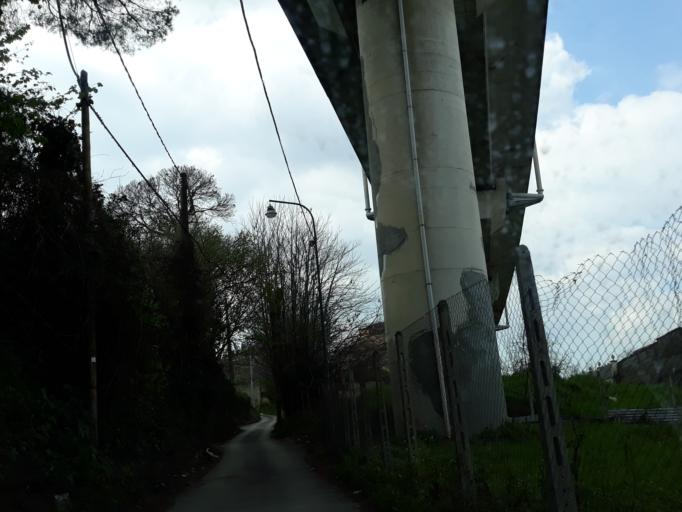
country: IT
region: Campania
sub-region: Provincia di Napoli
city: Napoli
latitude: 40.8829
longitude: 14.2287
